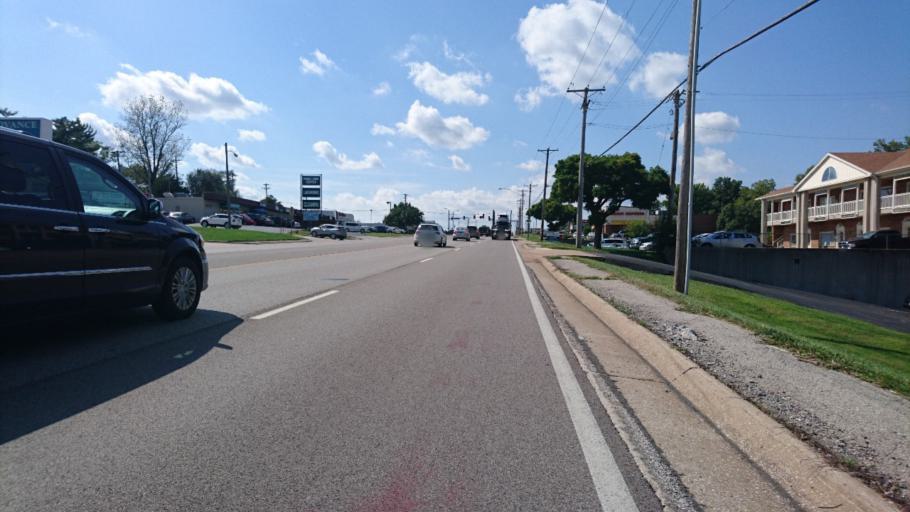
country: US
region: Missouri
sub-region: Saint Louis County
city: Winchester
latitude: 38.5931
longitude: -90.5276
